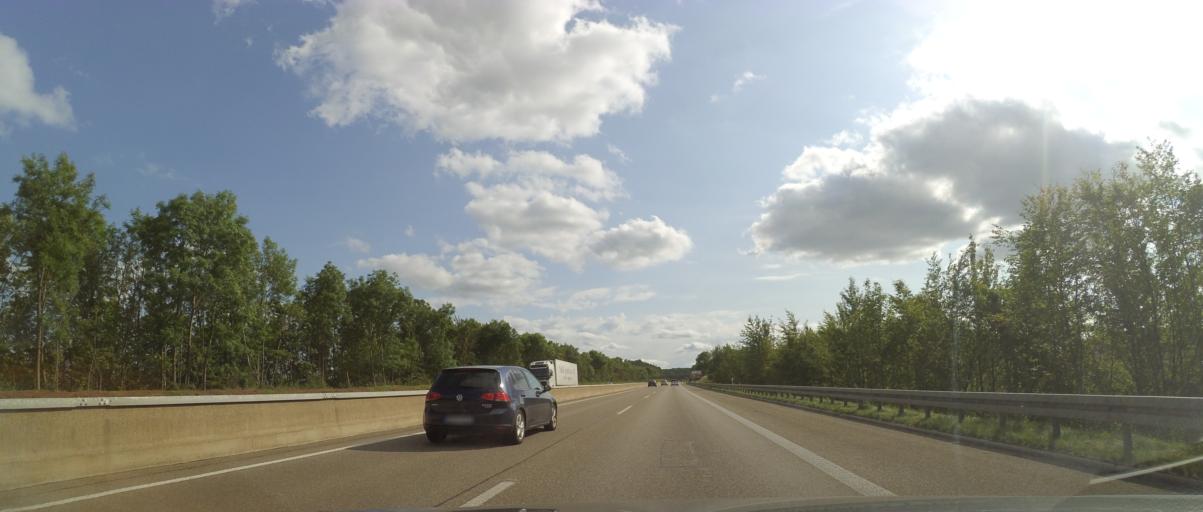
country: DE
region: North Rhine-Westphalia
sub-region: Regierungsbezirk Koln
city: Mechernich
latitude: 50.5465
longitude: 6.6782
